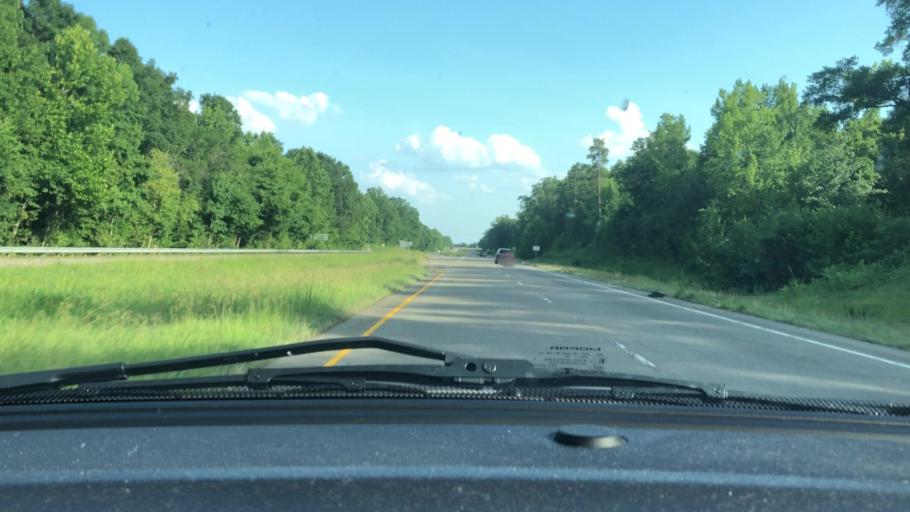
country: US
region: North Carolina
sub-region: Chatham County
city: Farmville
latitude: 35.5907
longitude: -79.3153
